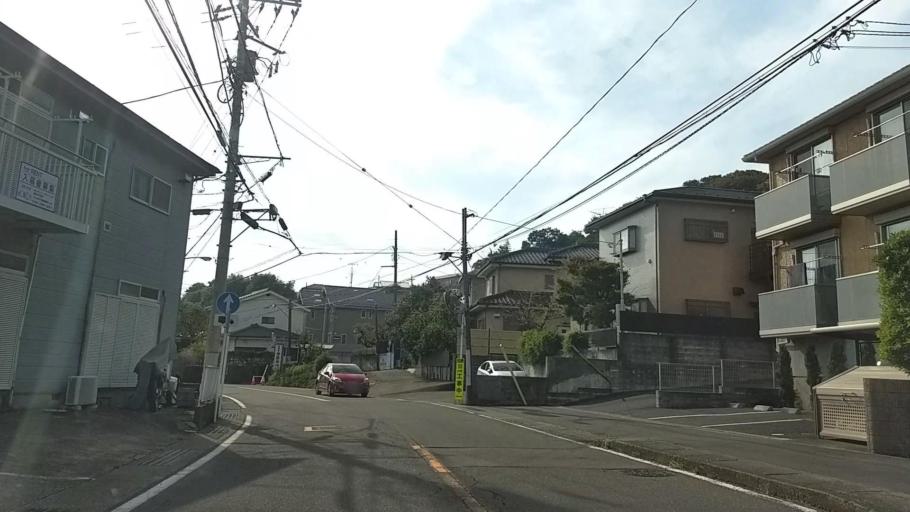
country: JP
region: Kanagawa
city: Atsugi
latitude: 35.4488
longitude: 139.3520
